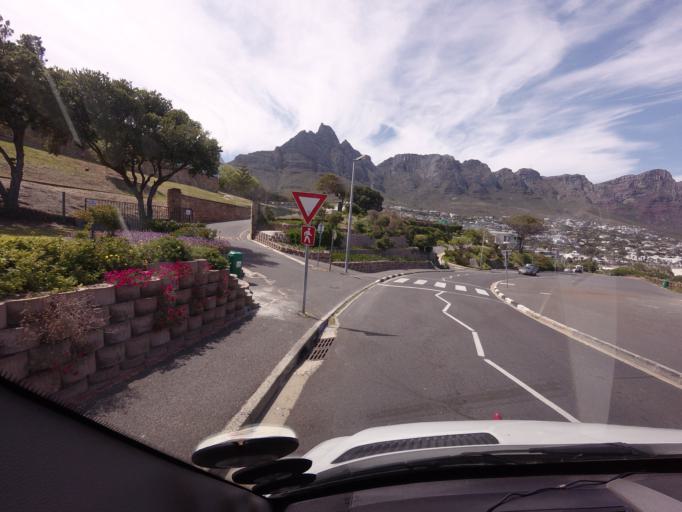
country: ZA
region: Western Cape
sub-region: City of Cape Town
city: Cape Town
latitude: -33.9452
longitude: 18.3777
